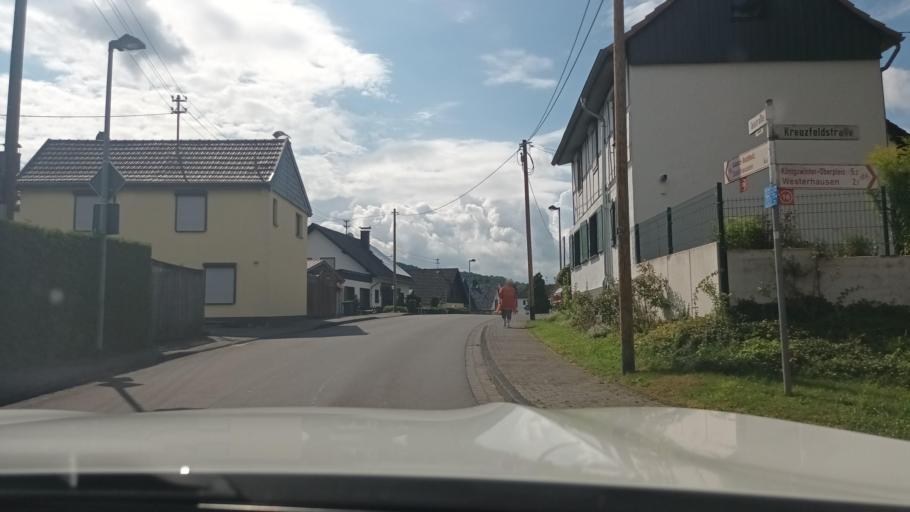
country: DE
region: North Rhine-Westphalia
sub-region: Regierungsbezirk Koln
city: Hennef
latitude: 50.7488
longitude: 7.3093
